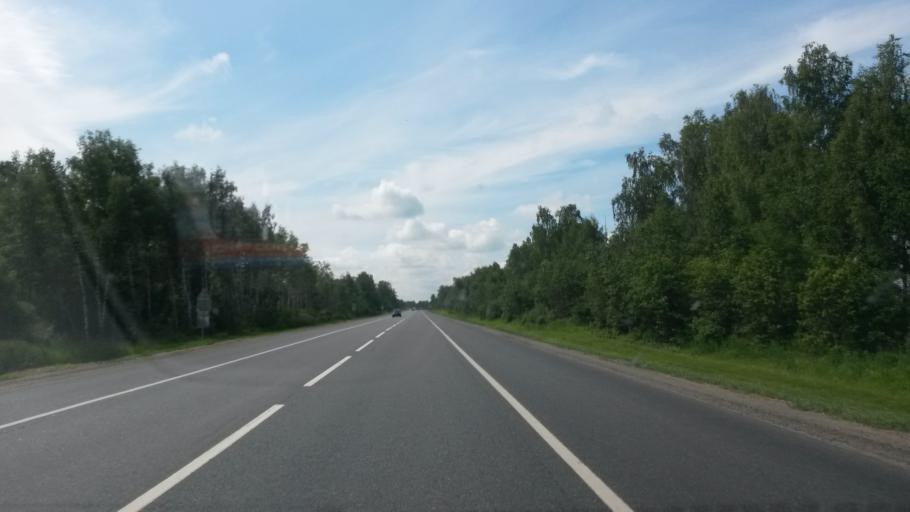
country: RU
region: Jaroslavl
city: Porech'ye-Rybnoye
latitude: 57.1217
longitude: 39.3217
